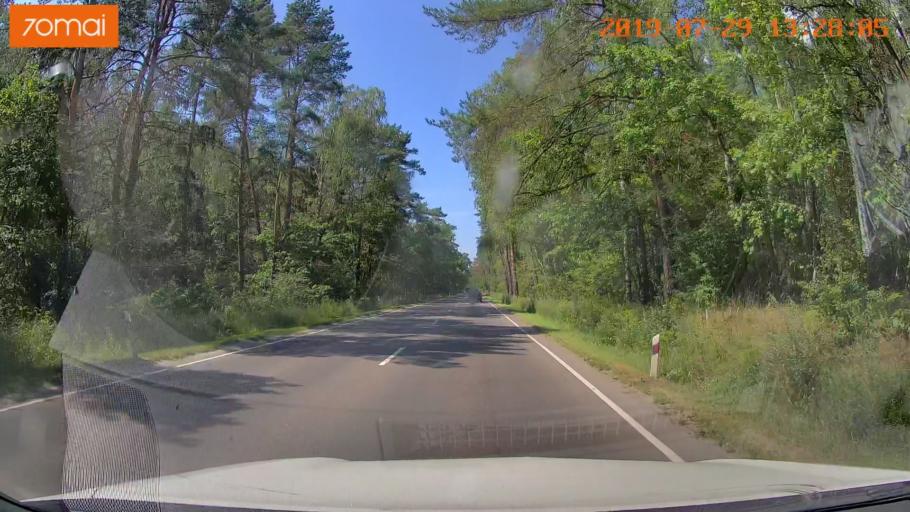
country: RU
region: Kaliningrad
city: Vzmorye
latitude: 54.7047
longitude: 20.2885
